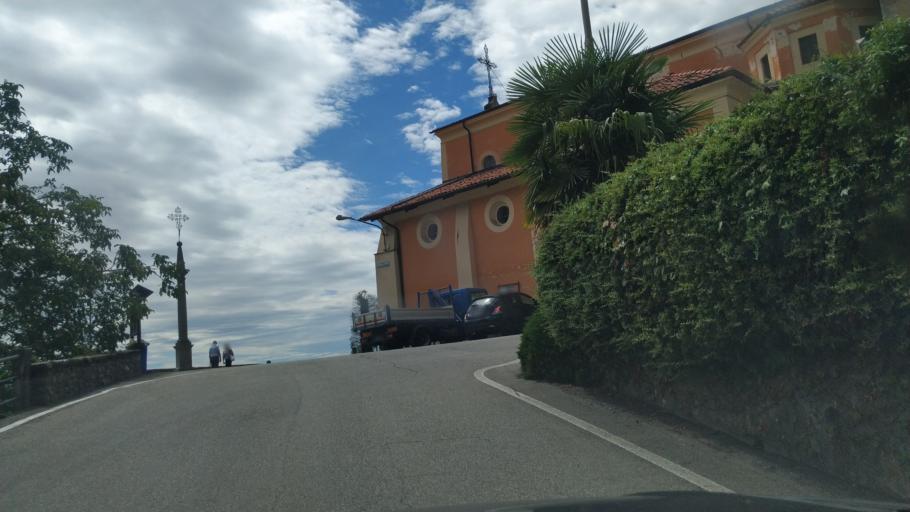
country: IT
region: Piedmont
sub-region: Provincia di Biella
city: Pollone
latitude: 45.5816
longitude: 7.9988
